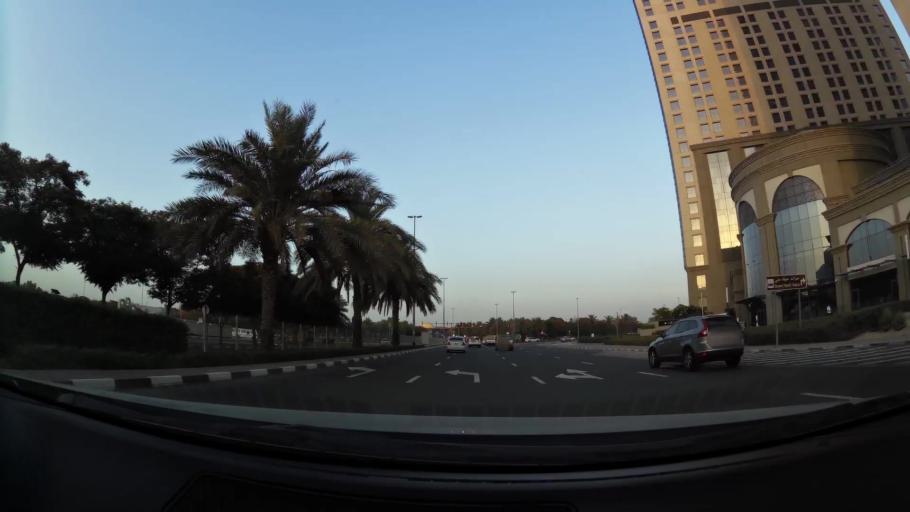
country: AE
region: Ash Shariqah
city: Sharjah
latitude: 25.2351
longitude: 55.3236
